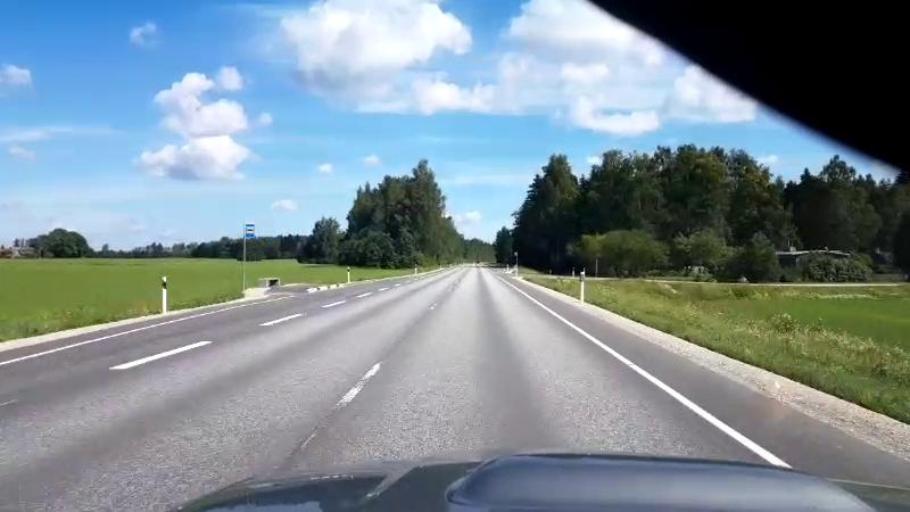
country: EE
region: Jaervamaa
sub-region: Paide linn
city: Paide
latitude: 58.9959
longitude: 25.6755
